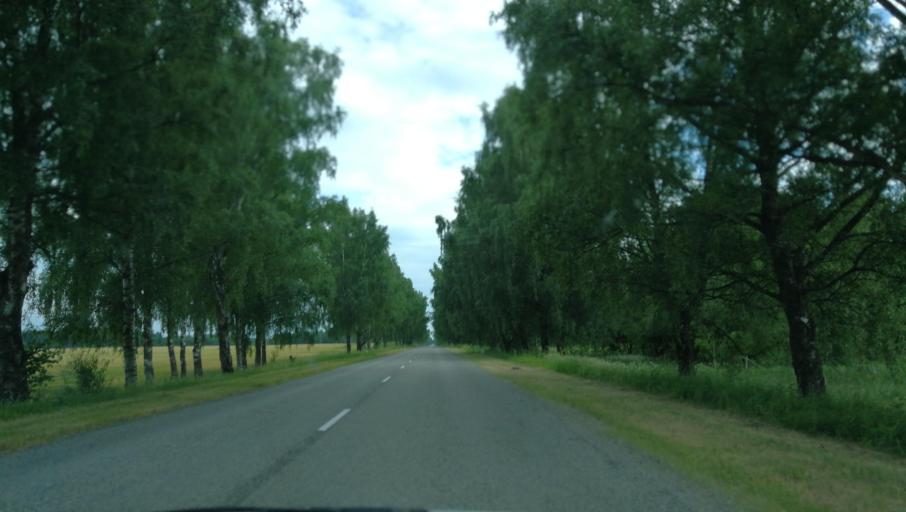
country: LV
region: Valmieras Rajons
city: Valmiera
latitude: 57.6309
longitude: 25.4477
